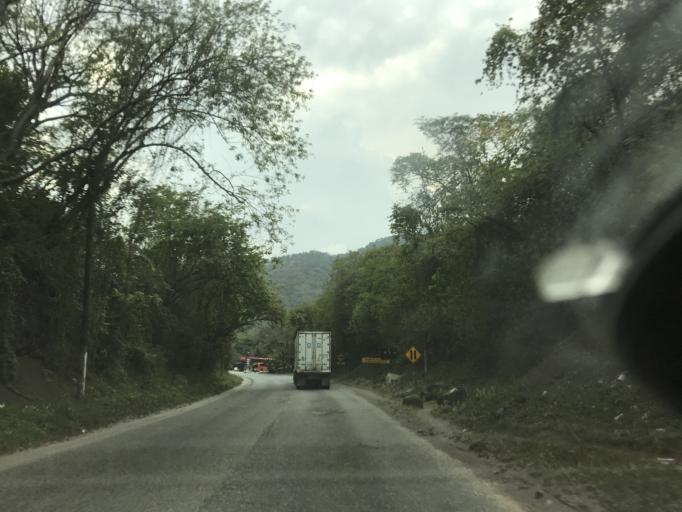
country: GT
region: Zacapa
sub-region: Municipio de Zacapa
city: Gualan
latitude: 15.2075
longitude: -89.2472
